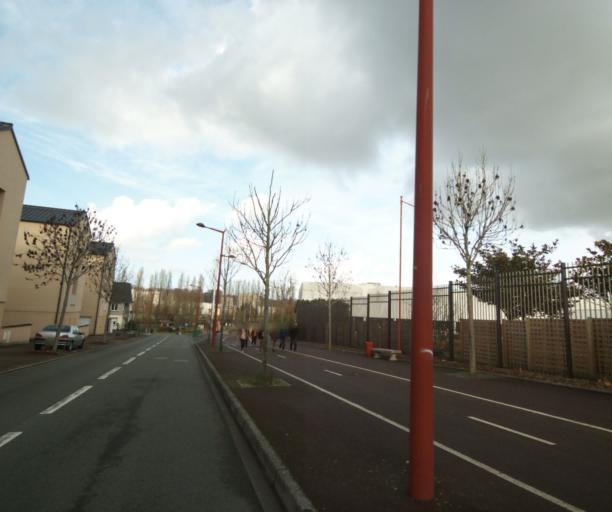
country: FR
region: Pays de la Loire
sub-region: Departement de la Sarthe
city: Le Mans
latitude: 47.9871
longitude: 0.2249
